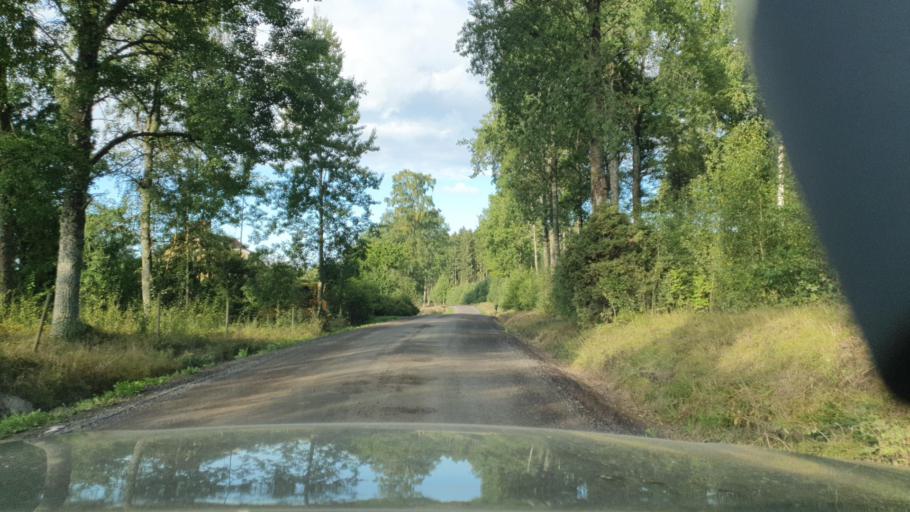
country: SE
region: Vaestra Goetaland
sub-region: Gullspangs Kommun
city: Gullspang
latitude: 59.1105
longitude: 14.0438
